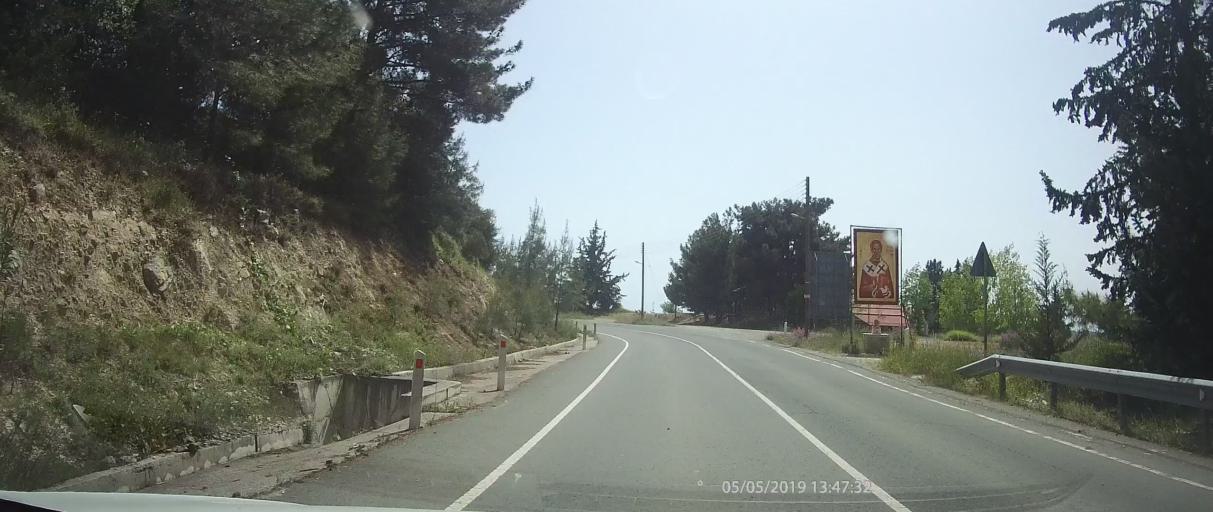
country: CY
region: Limassol
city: Pachna
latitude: 34.8650
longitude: 32.7561
